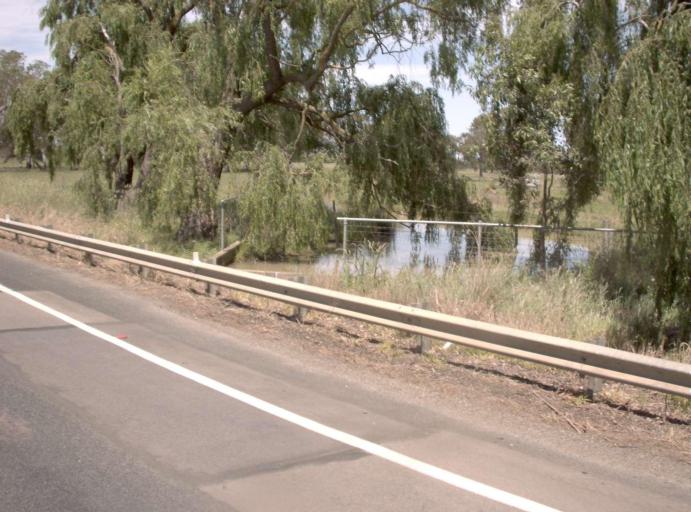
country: AU
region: Victoria
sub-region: Wellington
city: Heyfield
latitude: -38.1106
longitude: 146.8877
